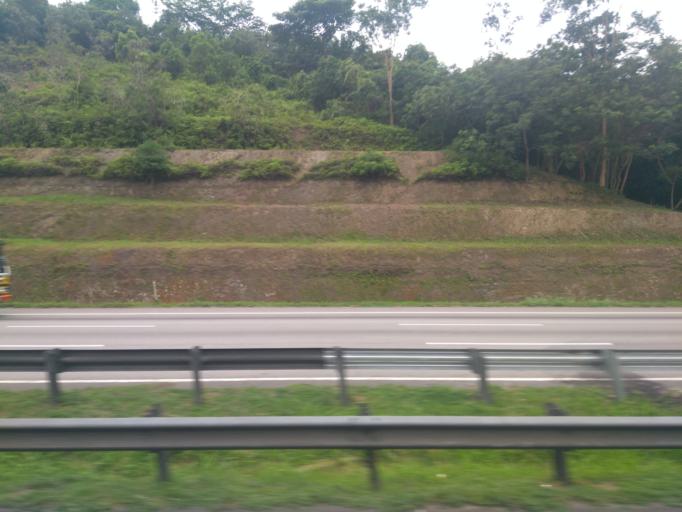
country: MY
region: Negeri Sembilan
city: Tampin
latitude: 2.4661
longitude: 102.1537
